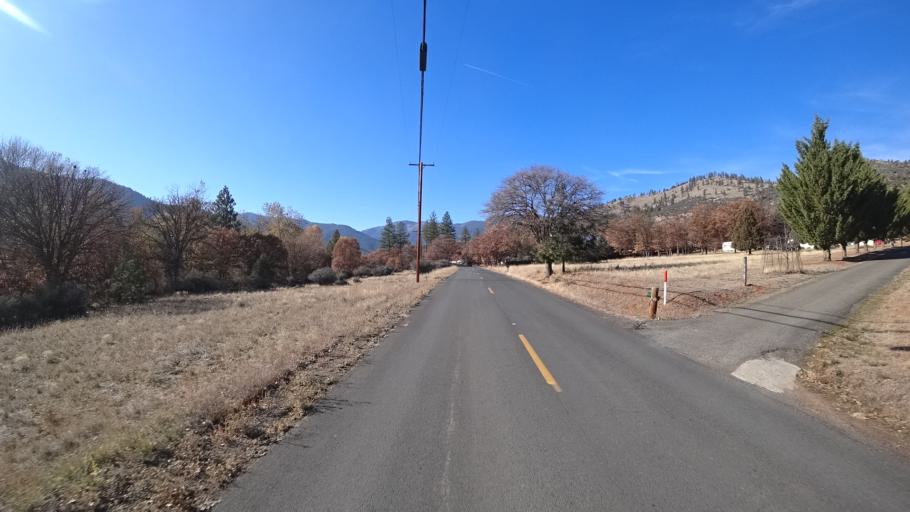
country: US
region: California
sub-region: Siskiyou County
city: Yreka
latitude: 41.7158
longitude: -122.6618
